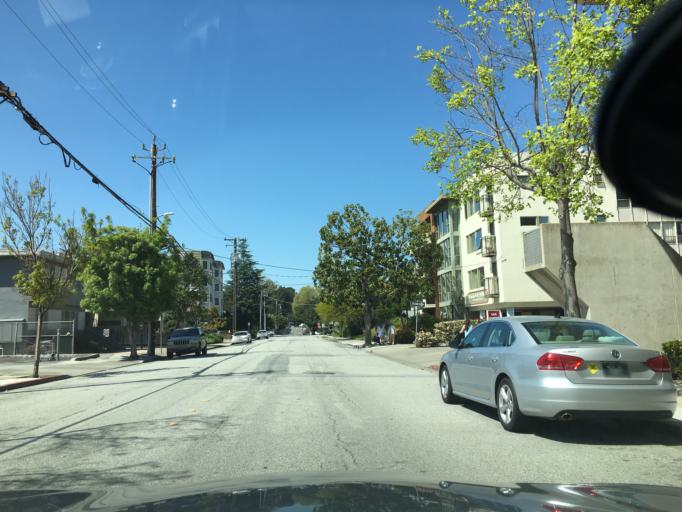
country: US
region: California
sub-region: San Mateo County
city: San Carlos
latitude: 37.5061
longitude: -122.2624
